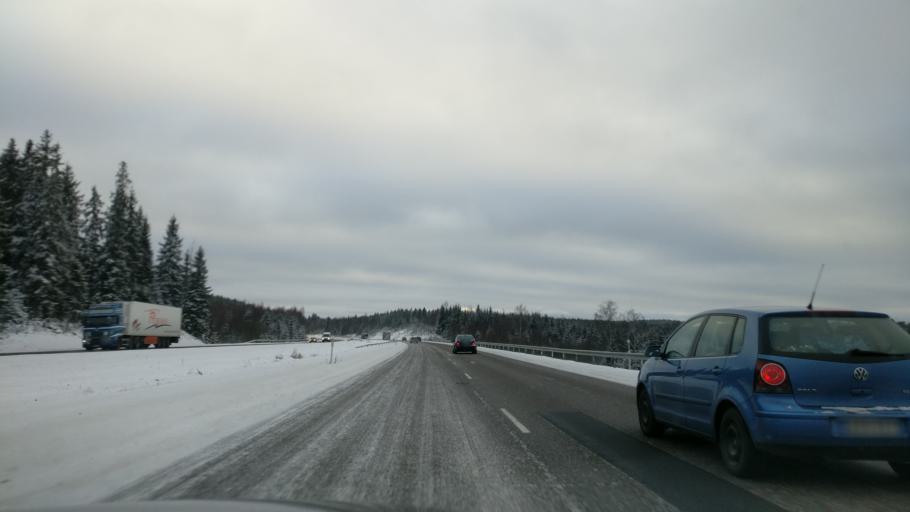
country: FI
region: Paijanne Tavastia
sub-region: Lahti
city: Nastola
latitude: 61.0307
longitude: 25.8376
